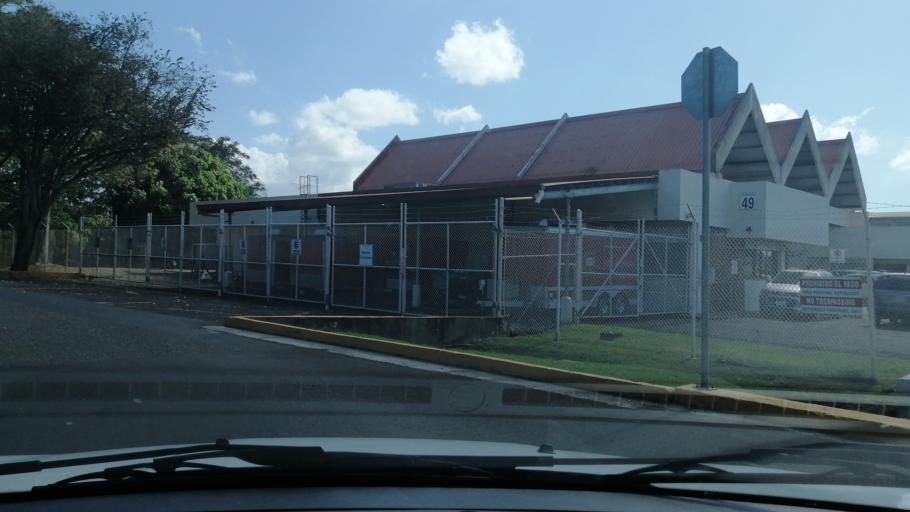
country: PA
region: Panama
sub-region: Distrito de Panama
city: Paraiso
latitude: 8.9973
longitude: -79.5902
